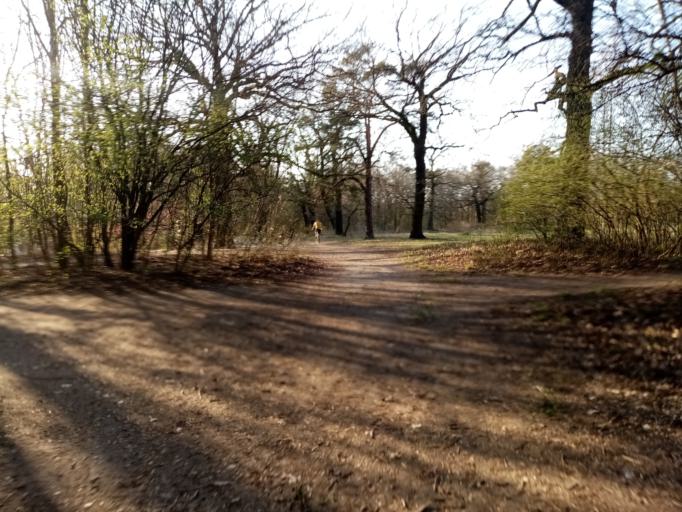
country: DE
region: Berlin
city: Oberschoneweide
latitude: 52.4668
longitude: 13.5360
